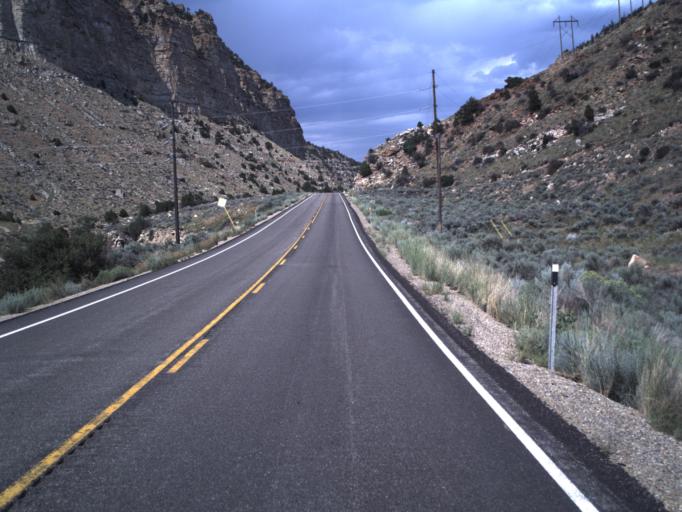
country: US
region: Utah
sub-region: Carbon County
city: Helper
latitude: 39.7341
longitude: -110.8490
